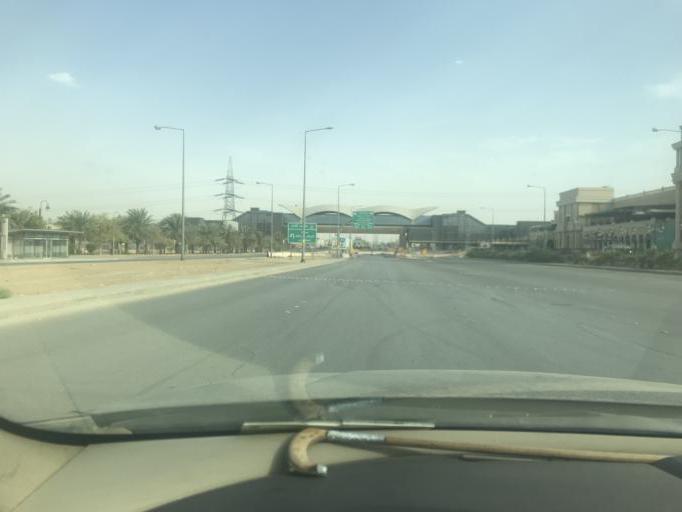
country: SA
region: Ar Riyad
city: Riyadh
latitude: 24.8040
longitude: 46.6947
